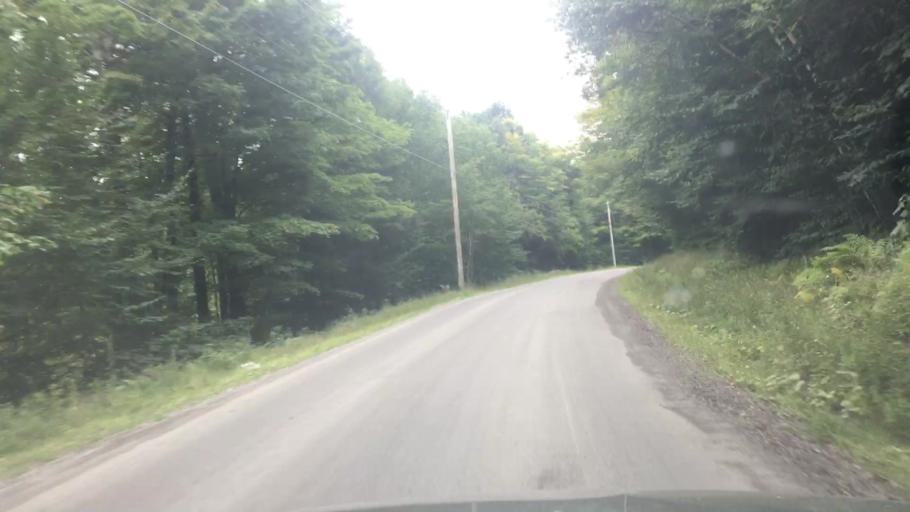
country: US
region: Vermont
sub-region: Windham County
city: Dover
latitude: 42.8372
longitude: -72.8145
